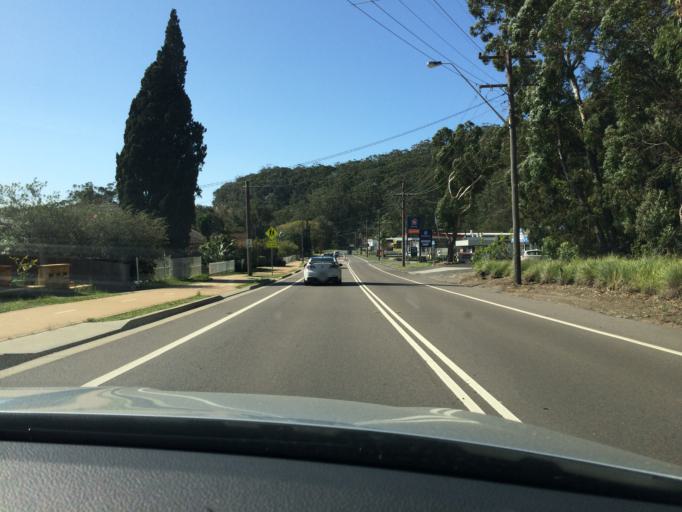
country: AU
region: New South Wales
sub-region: Gosford Shire
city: Ettalong Beach
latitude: -33.5081
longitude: 151.3310
